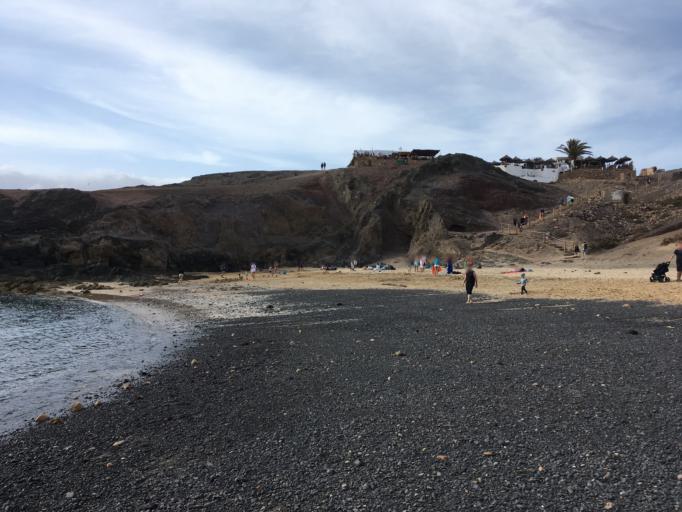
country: ES
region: Canary Islands
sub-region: Provincia de Las Palmas
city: Playa Blanca
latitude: 28.8424
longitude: -13.7883
